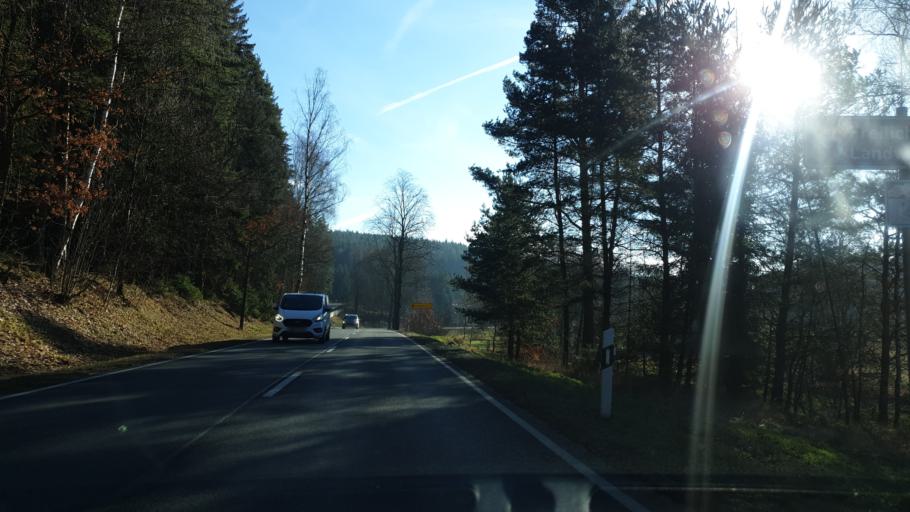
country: DE
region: Saxony
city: Markneukirchen
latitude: 50.2697
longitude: 12.2988
